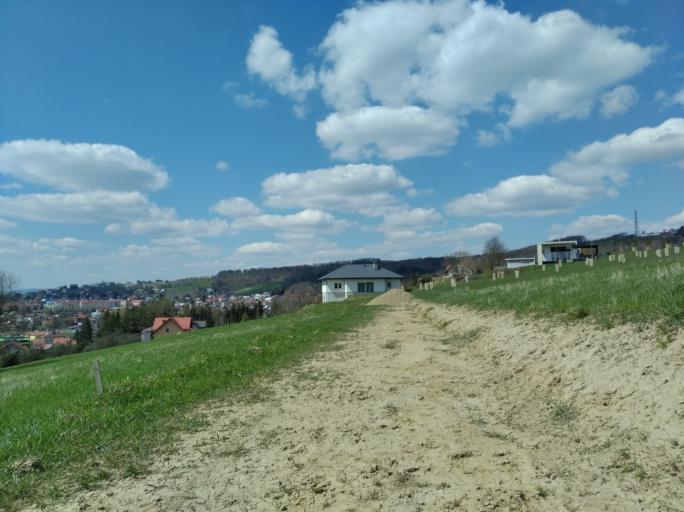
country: PL
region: Subcarpathian Voivodeship
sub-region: Powiat strzyzowski
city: Strzyzow
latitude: 49.8711
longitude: 21.8085
